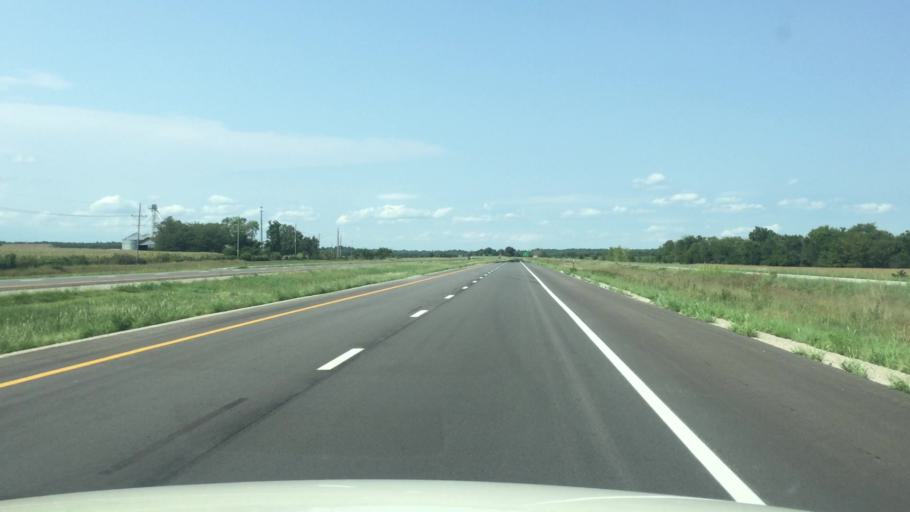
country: US
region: Kansas
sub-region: Linn County
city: La Cygne
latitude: 38.3262
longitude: -94.6774
